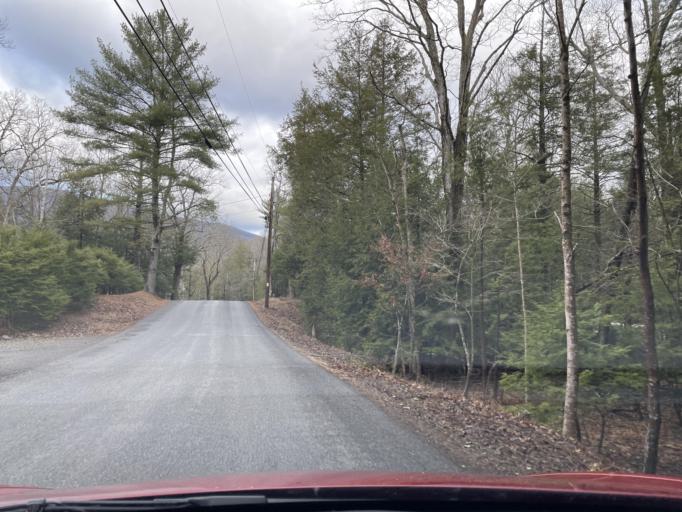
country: US
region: New York
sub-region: Ulster County
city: Manorville
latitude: 42.0830
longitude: -74.0437
